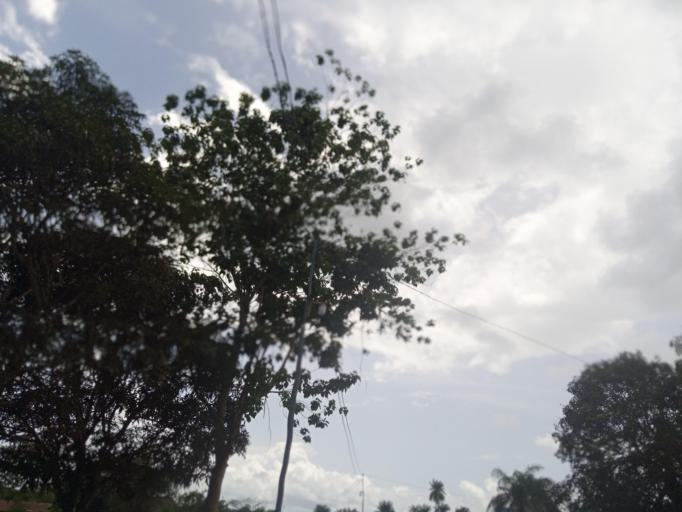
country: SL
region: Northern Province
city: Sawkta
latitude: 8.6327
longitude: -13.2038
